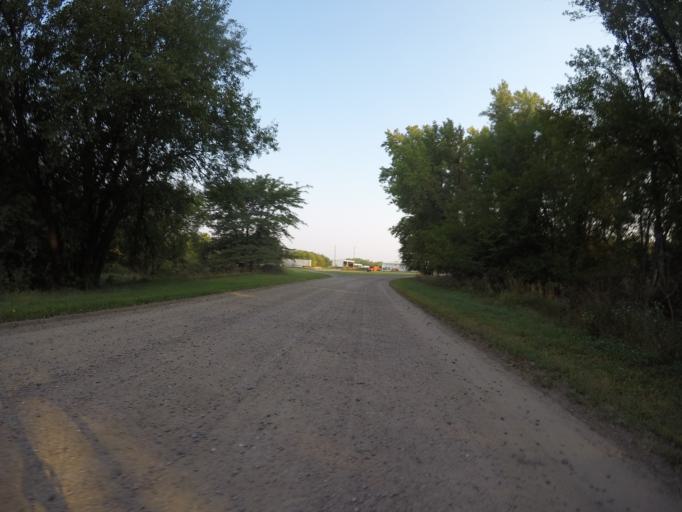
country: US
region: Kansas
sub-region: Marshall County
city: Marysville
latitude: 39.8578
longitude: -96.6527
